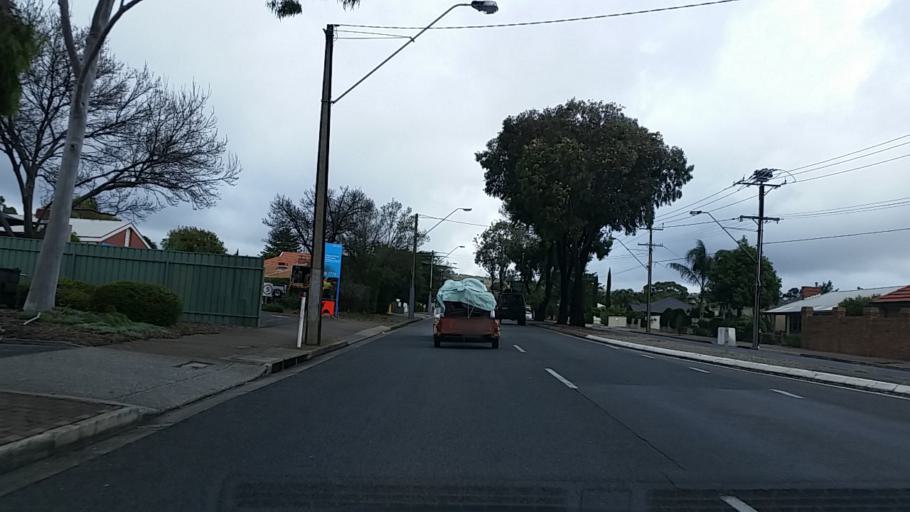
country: AU
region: South Australia
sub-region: Marion
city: Sturt
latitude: -35.0192
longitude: 138.5500
